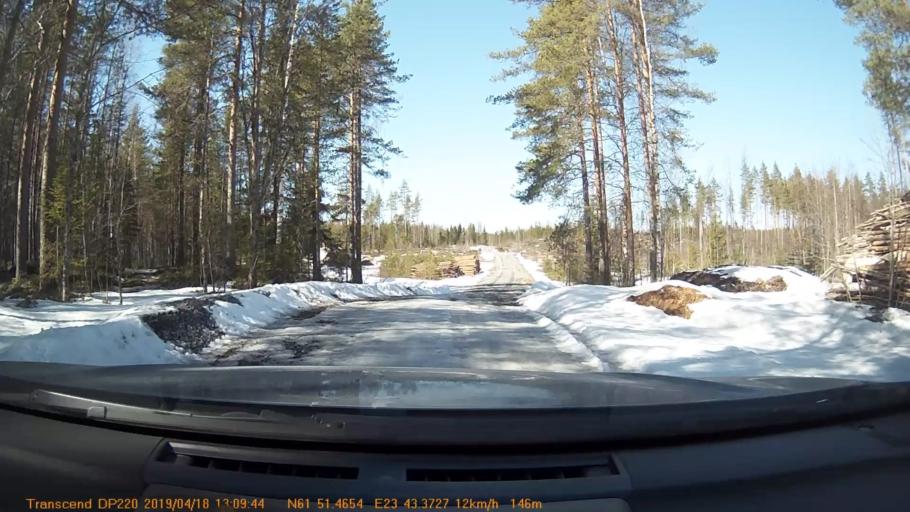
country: FI
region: Pirkanmaa
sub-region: Tampere
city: Kuru
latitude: 61.8577
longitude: 23.7230
